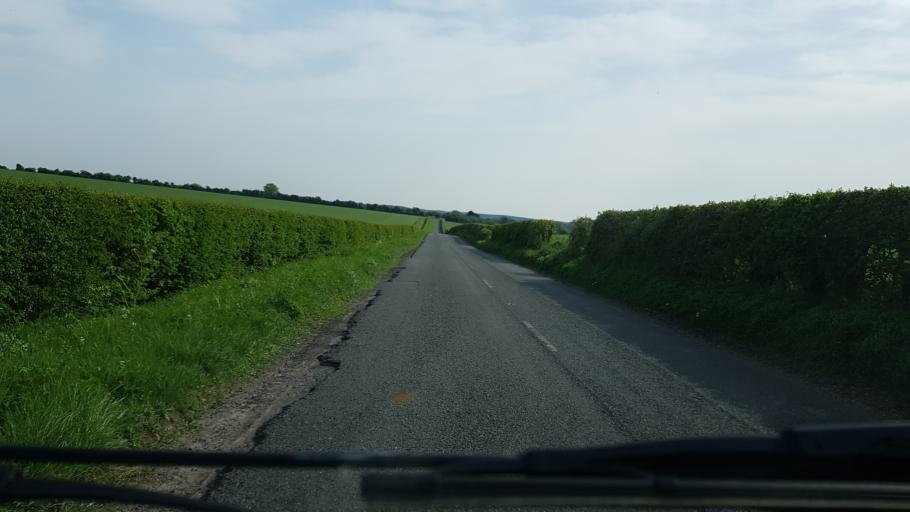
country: GB
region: England
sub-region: Hampshire
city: Overton
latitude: 51.2687
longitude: -1.2640
